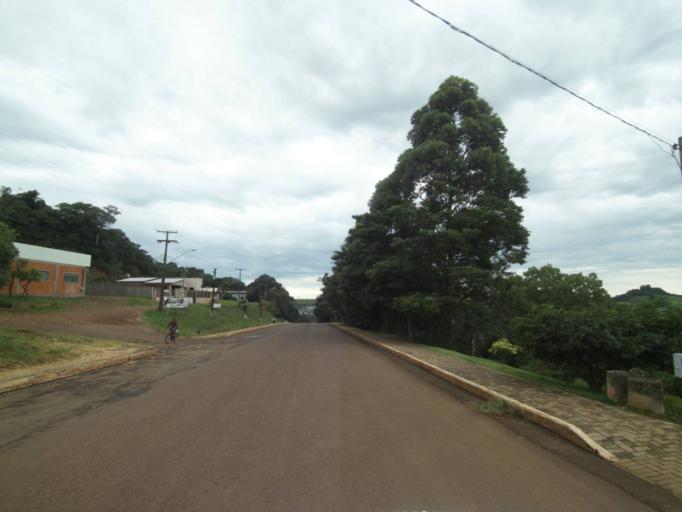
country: BR
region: Parana
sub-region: Guaraniacu
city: Guaraniacu
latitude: -25.1052
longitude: -52.8598
